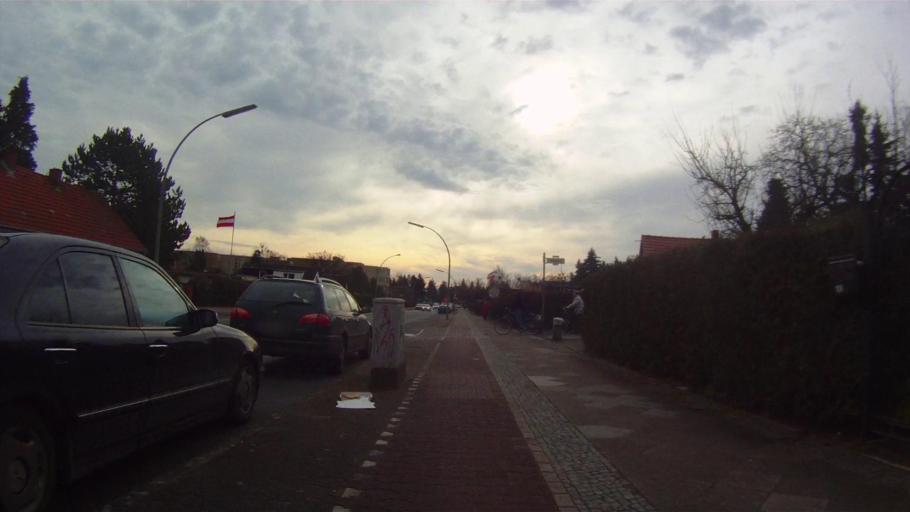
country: DE
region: Berlin
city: Lichtenrade
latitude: 52.4202
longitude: 13.4156
